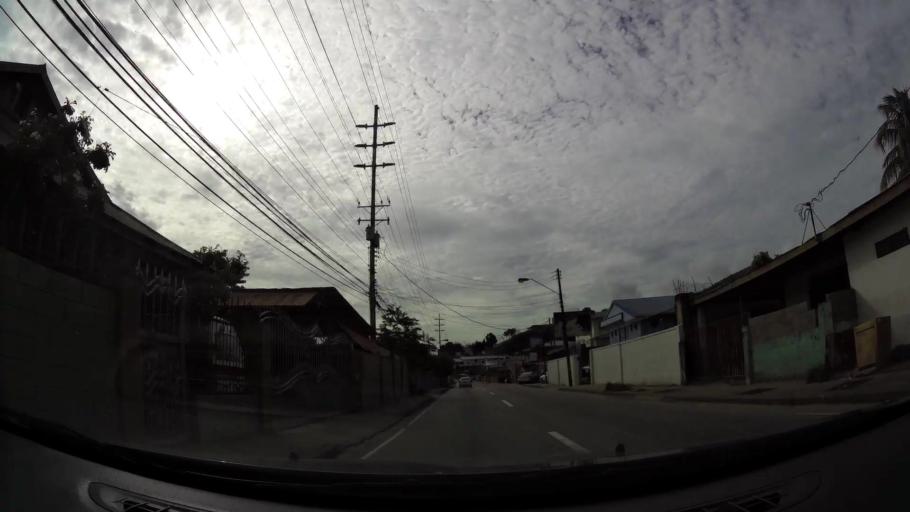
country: TT
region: City of Port of Spain
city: Mucurapo
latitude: 10.6806
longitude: -61.5741
